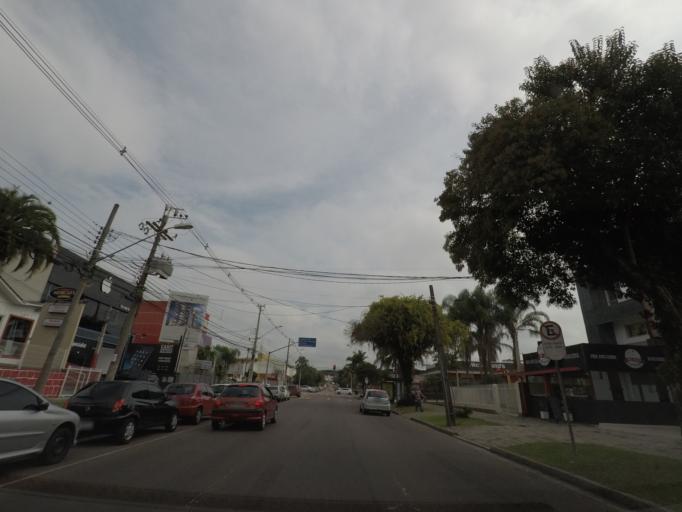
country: BR
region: Parana
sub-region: Curitiba
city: Curitiba
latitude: -25.4520
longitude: -49.2688
